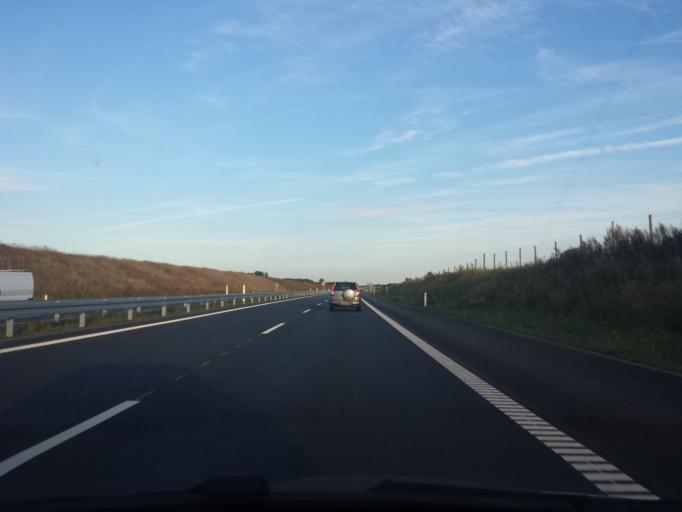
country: DK
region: Capital Region
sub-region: Ballerup Kommune
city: Ballerup
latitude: 55.7124
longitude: 12.3357
